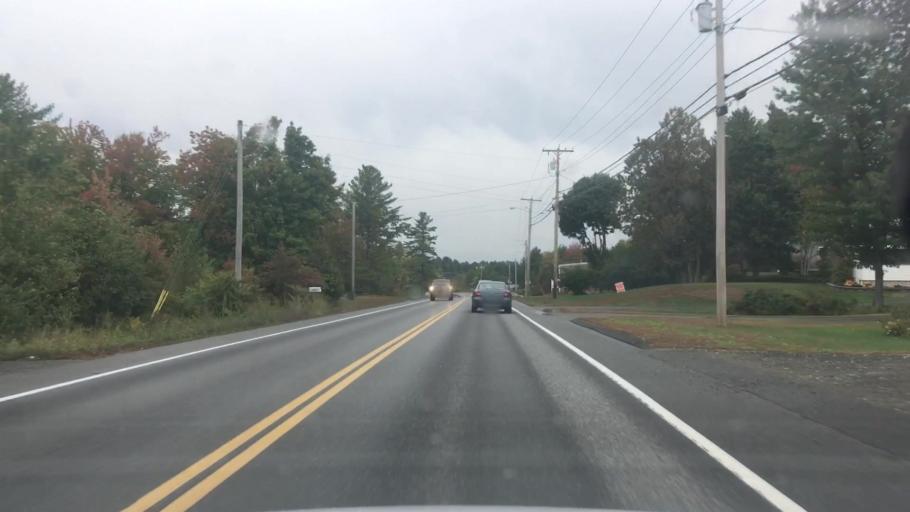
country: US
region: Maine
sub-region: Kennebec County
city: Augusta
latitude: 44.3655
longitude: -69.7882
